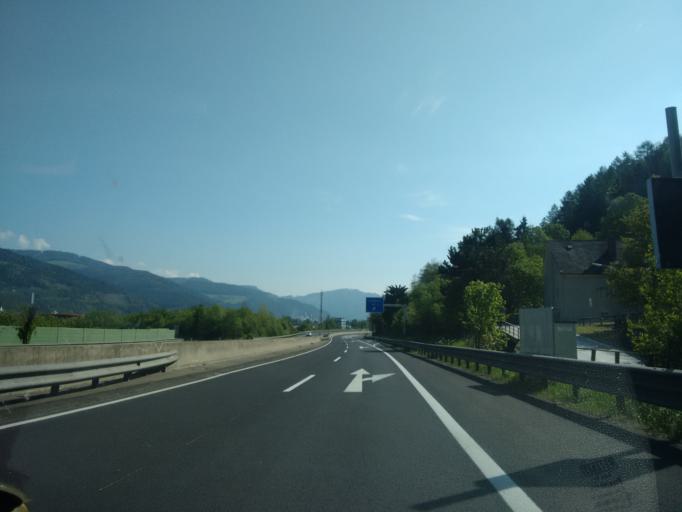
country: AT
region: Styria
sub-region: Politischer Bezirk Leoben
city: Proleb
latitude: 47.3819
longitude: 15.1225
